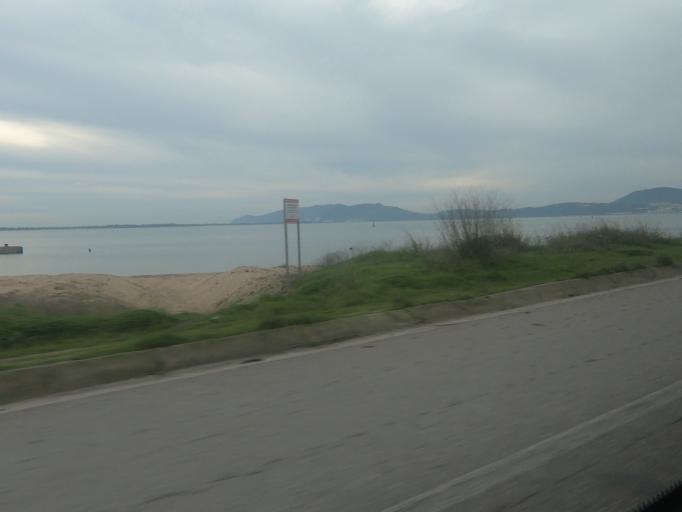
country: PT
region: Setubal
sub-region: Setubal
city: Setubal
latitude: 38.5022
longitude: -8.8421
